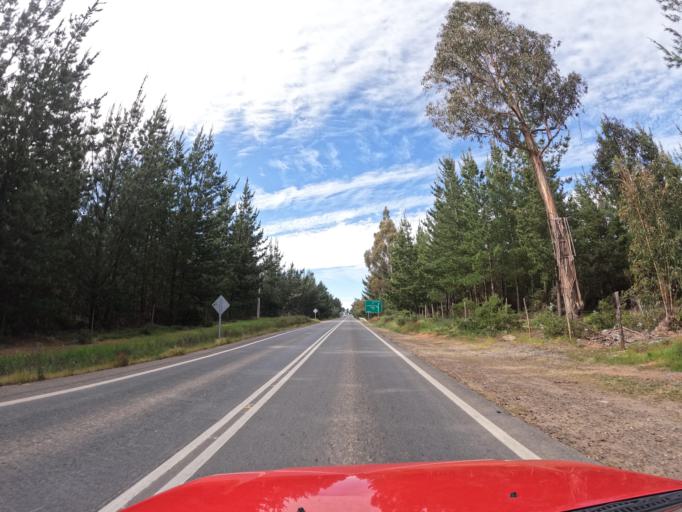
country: CL
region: O'Higgins
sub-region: Provincia de Colchagua
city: Santa Cruz
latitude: -34.3130
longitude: -71.8523
